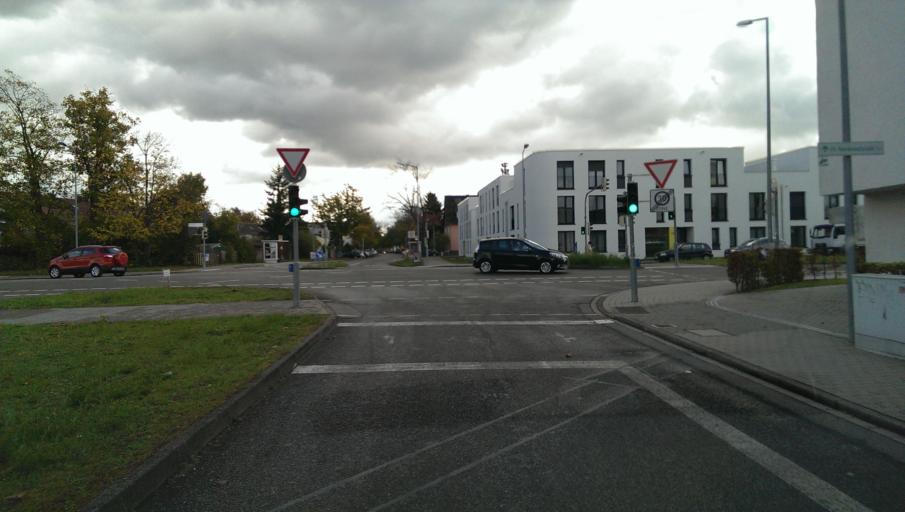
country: DE
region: Baden-Wuerttemberg
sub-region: Karlsruhe Region
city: Karlsruhe
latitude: 49.0356
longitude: 8.3505
